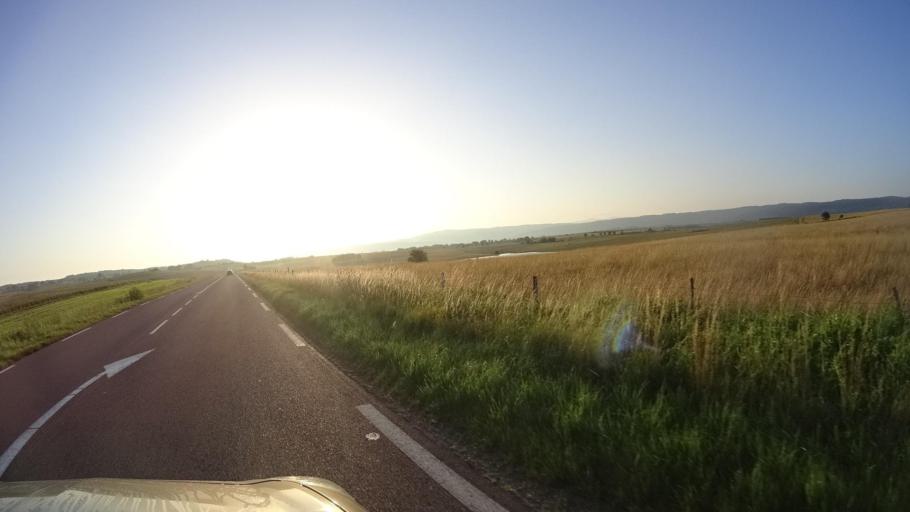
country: FR
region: Franche-Comte
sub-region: Departement du Doubs
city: Frasne
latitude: 46.9007
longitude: 6.2487
